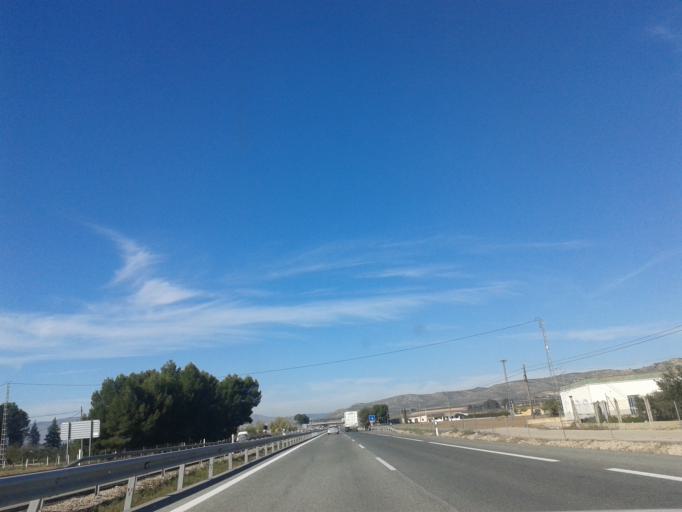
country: ES
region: Valencia
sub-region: Provincia de Alicante
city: Villena
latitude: 38.6658
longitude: -0.8817
